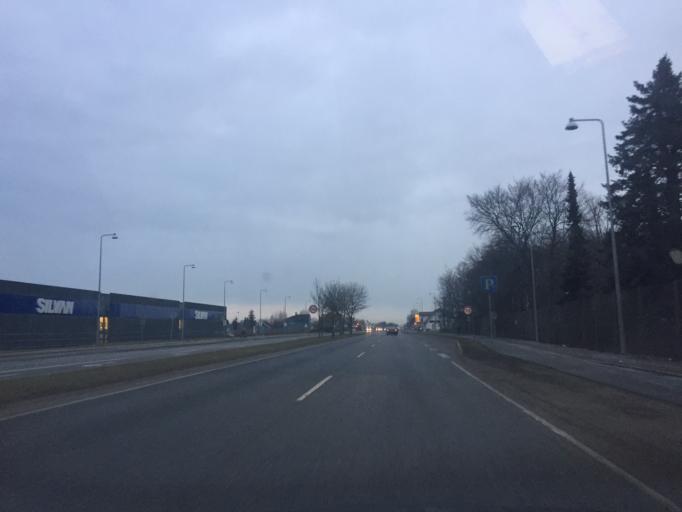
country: DK
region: Zealand
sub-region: Koge Kommune
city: Koge
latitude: 55.4824
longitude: 12.1868
